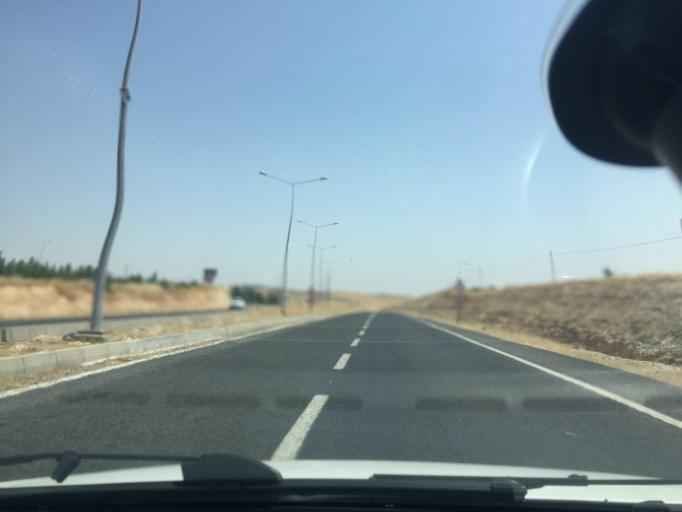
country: TR
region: Mardin
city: Acirli
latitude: 37.4400
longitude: 41.2939
